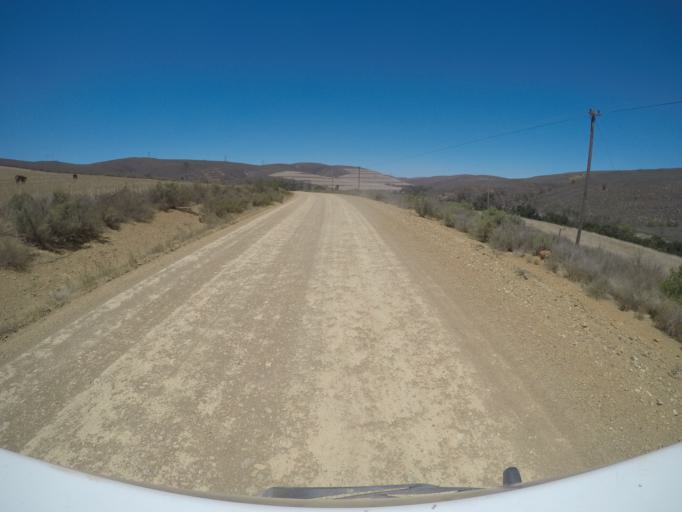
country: ZA
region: Western Cape
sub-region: Overberg District Municipality
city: Caledon
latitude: -34.1346
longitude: 19.2436
